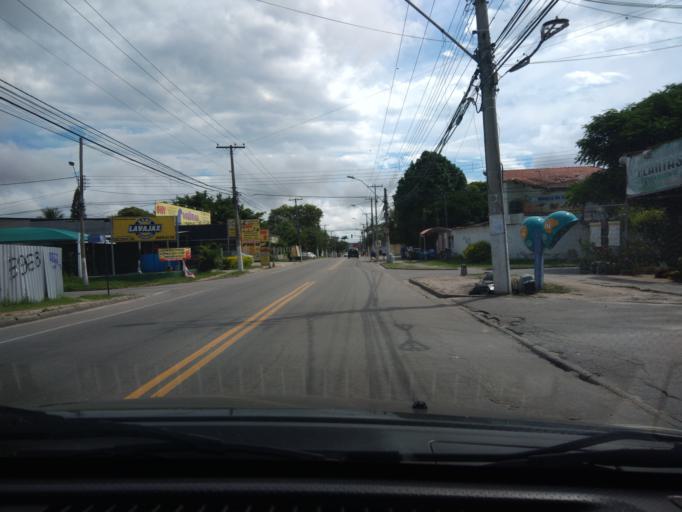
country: BR
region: Rio de Janeiro
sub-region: Niteroi
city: Niteroi
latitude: -22.9301
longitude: -43.0161
